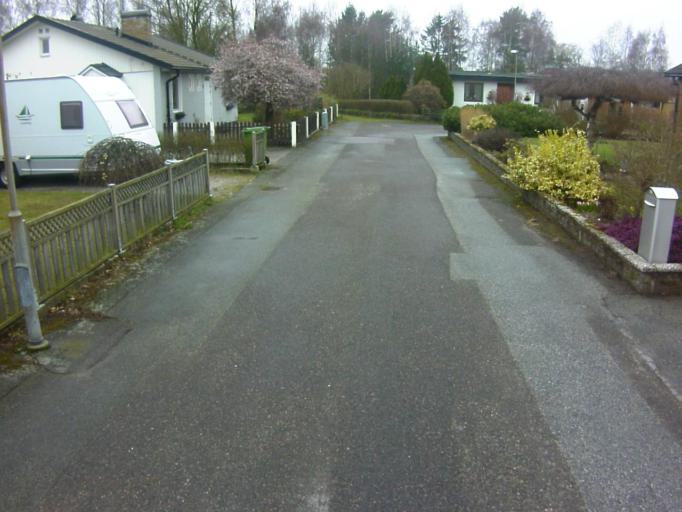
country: SE
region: Skane
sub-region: Kavlinge Kommun
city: Kaevlinge
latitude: 55.7799
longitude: 13.0853
